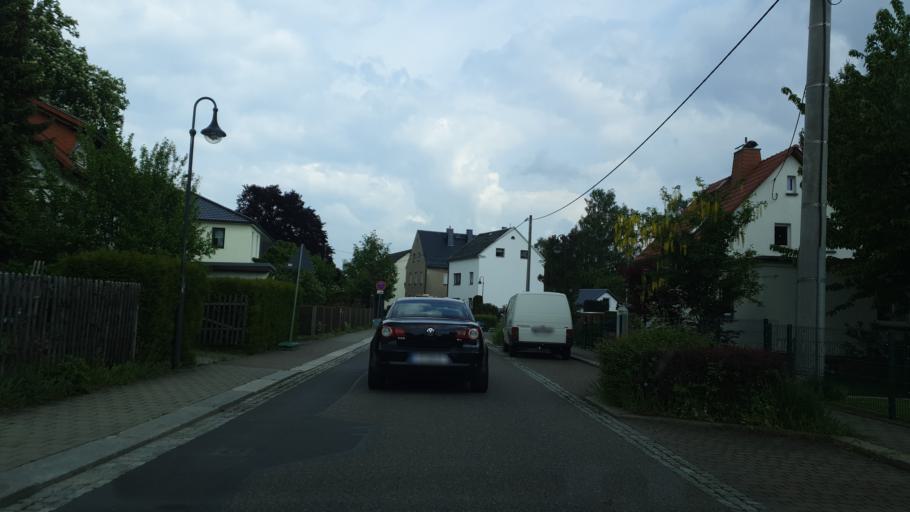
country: DE
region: Saxony
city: Wittgensdorf
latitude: 50.8618
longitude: 12.8535
